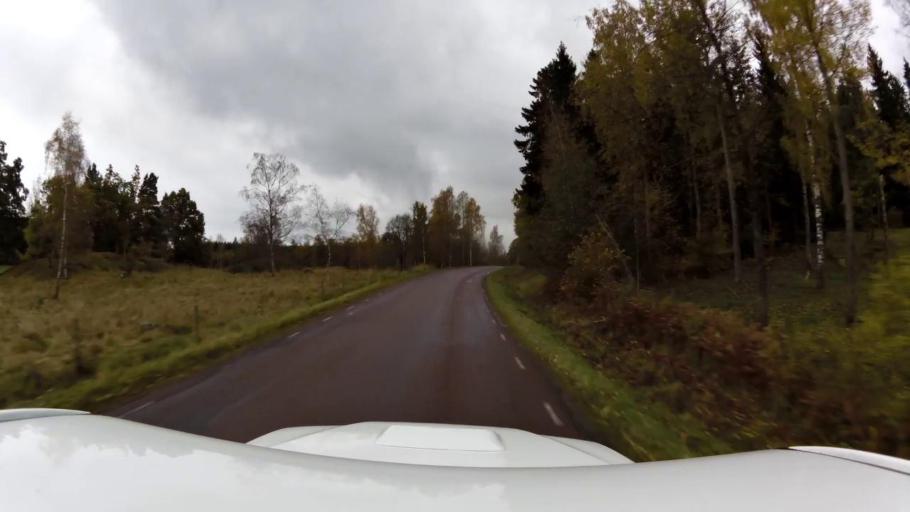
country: SE
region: OEstergoetland
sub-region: Linkopings Kommun
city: Ljungsbro
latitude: 58.5400
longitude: 15.5254
